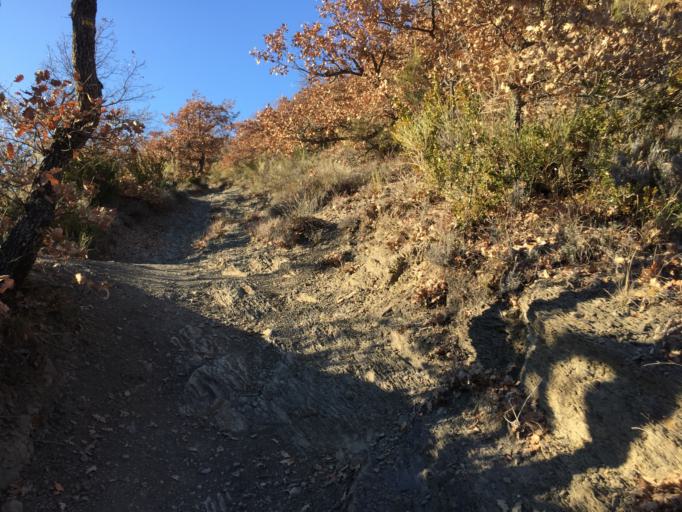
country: FR
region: Provence-Alpes-Cote d'Azur
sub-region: Departement des Alpes-de-Haute-Provence
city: Digne-les-Bains
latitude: 44.0815
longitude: 6.2647
